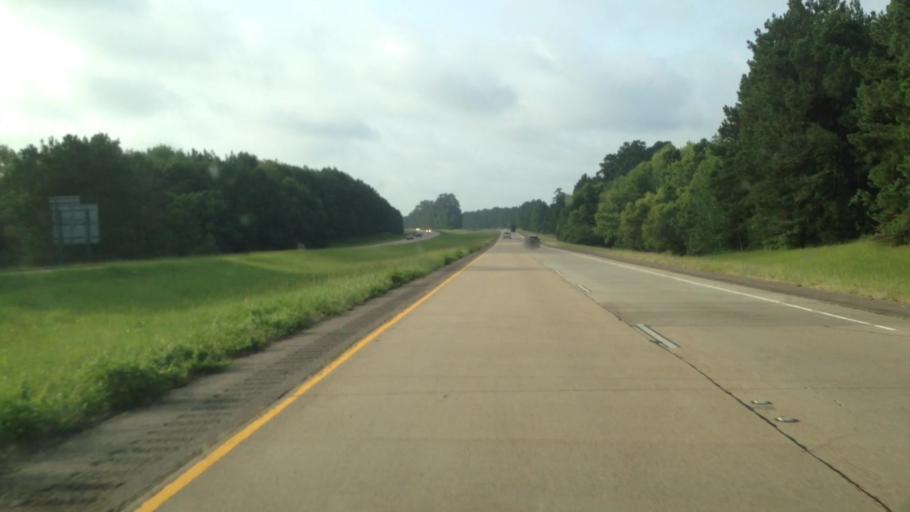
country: US
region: Louisiana
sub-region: Rapides Parish
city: Lecompte
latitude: 31.0428
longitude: -92.4175
